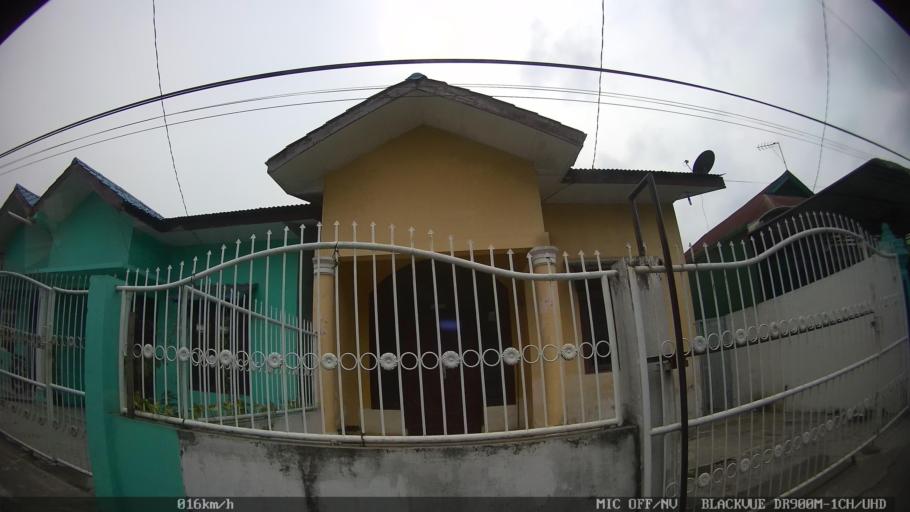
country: ID
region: North Sumatra
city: Medan
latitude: 3.5772
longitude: 98.7323
